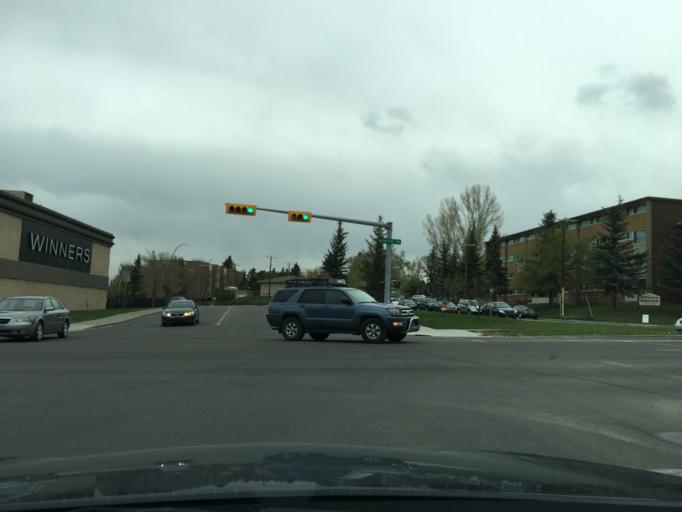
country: CA
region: Alberta
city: Calgary
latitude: 50.9794
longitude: -114.0680
